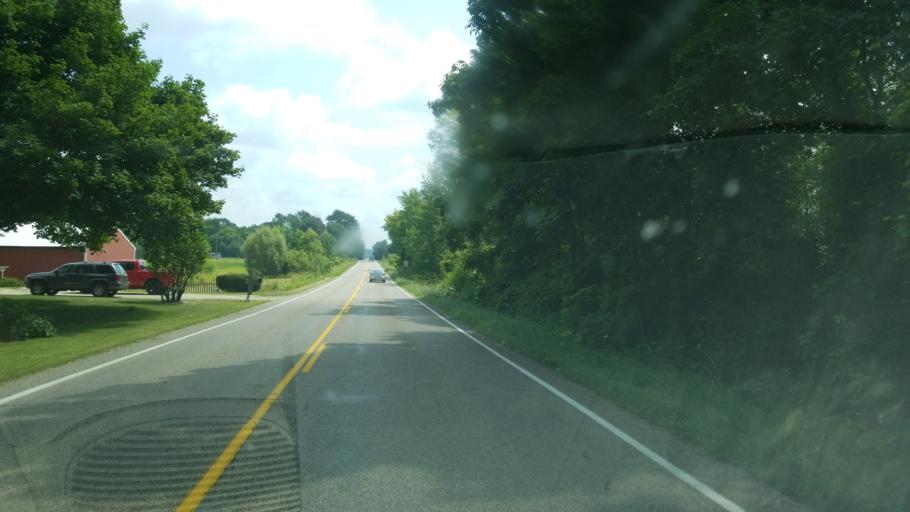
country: US
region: Michigan
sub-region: Kent County
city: Cedar Springs
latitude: 43.2202
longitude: -85.5359
